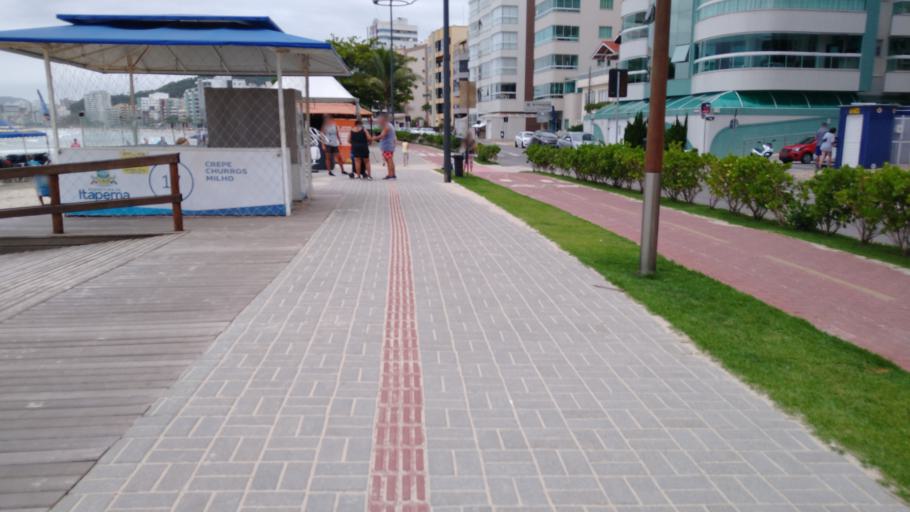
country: BR
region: Santa Catarina
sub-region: Itapema
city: Itapema
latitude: -27.0979
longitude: -48.6138
